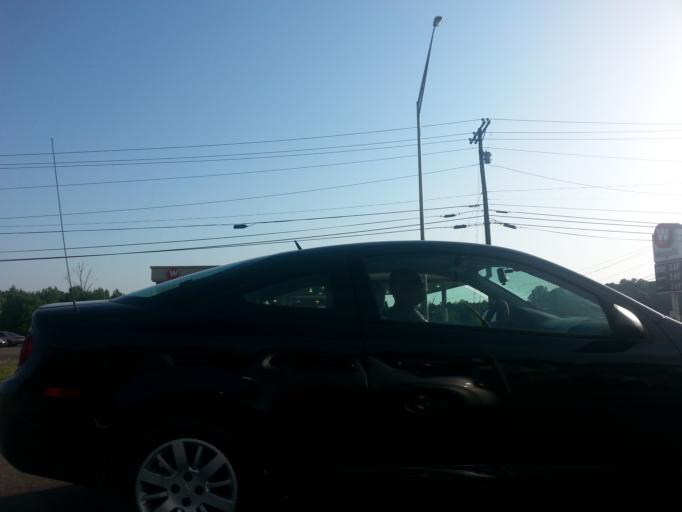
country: US
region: Tennessee
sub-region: Loudon County
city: Lenoir City
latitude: 35.8021
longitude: -84.2604
